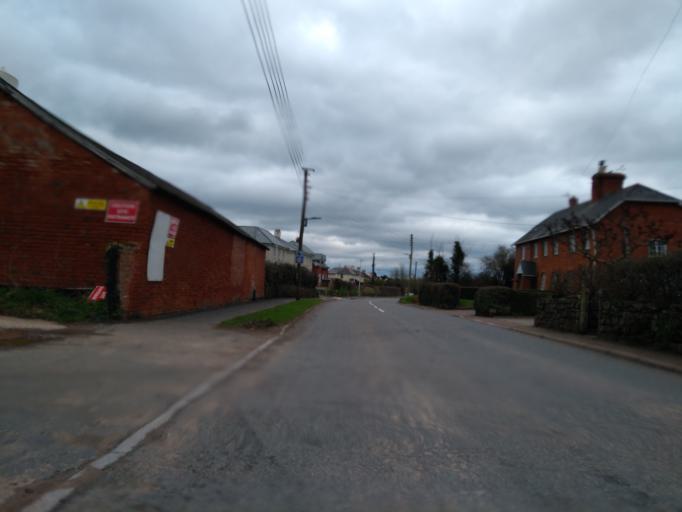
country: GB
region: England
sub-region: Devon
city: Exeter
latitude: 50.8072
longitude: -3.5222
